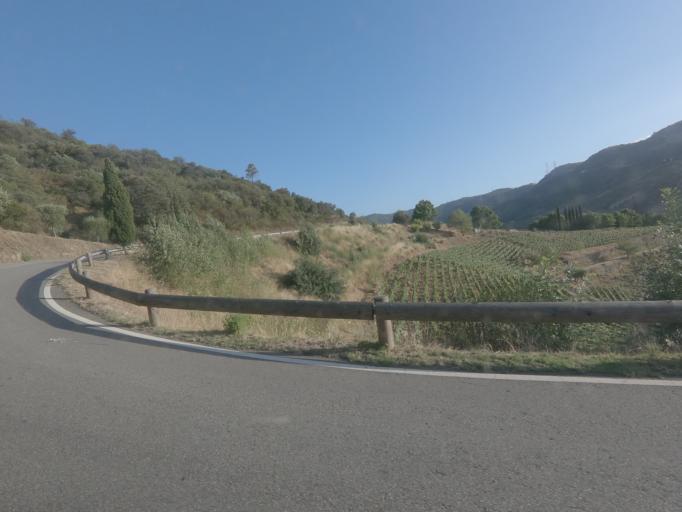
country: PT
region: Viseu
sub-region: Armamar
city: Armamar
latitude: 41.1539
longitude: -7.6368
